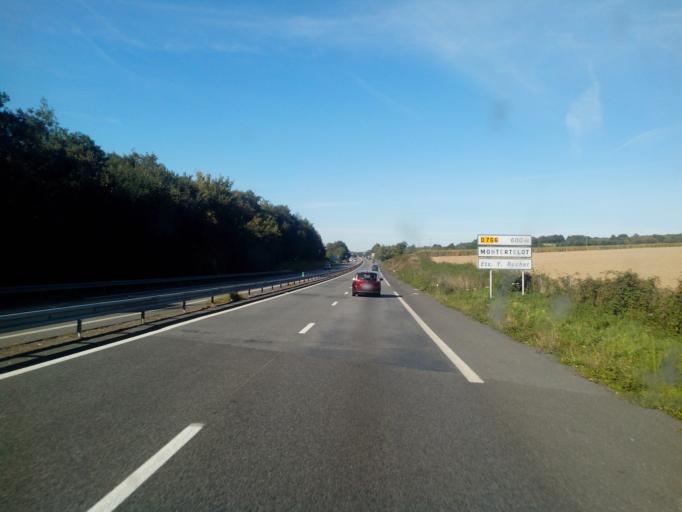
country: FR
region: Brittany
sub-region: Departement du Morbihan
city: Ploermel
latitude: 47.8764
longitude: -2.4176
